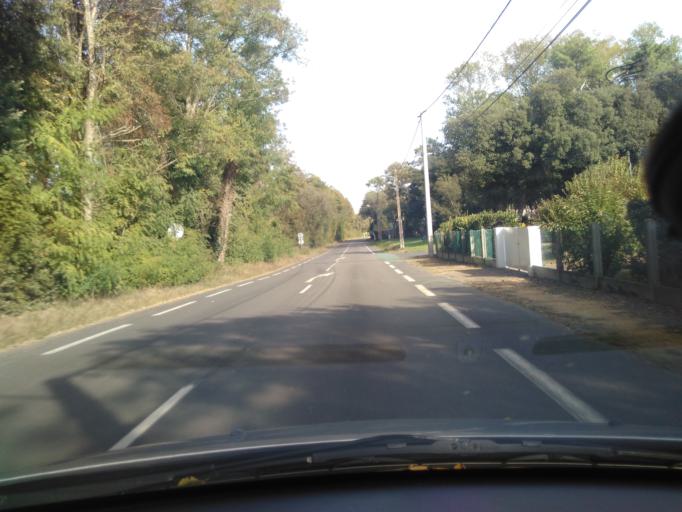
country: FR
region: Pays de la Loire
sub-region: Departement de la Vendee
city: Jard-sur-Mer
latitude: 46.4222
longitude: -1.6141
